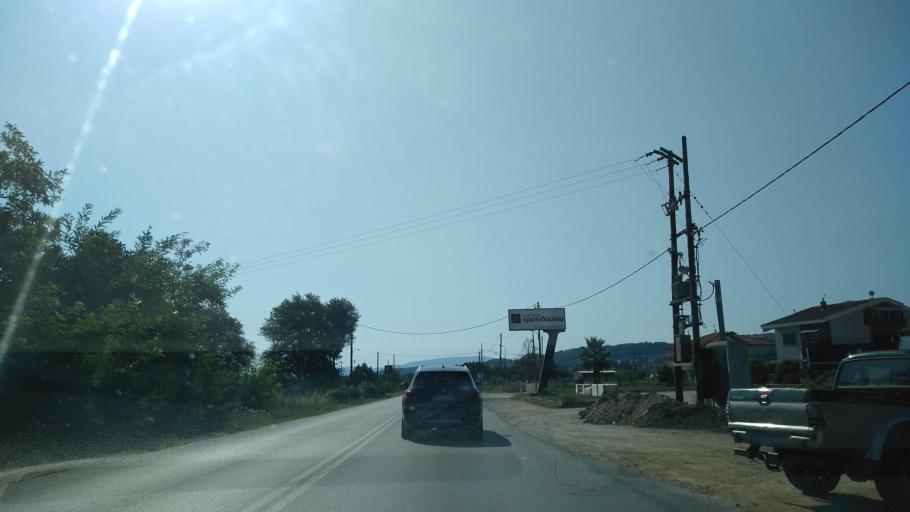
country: GR
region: Central Macedonia
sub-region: Nomos Chalkidikis
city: Ierissos
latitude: 40.4023
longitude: 23.8663
